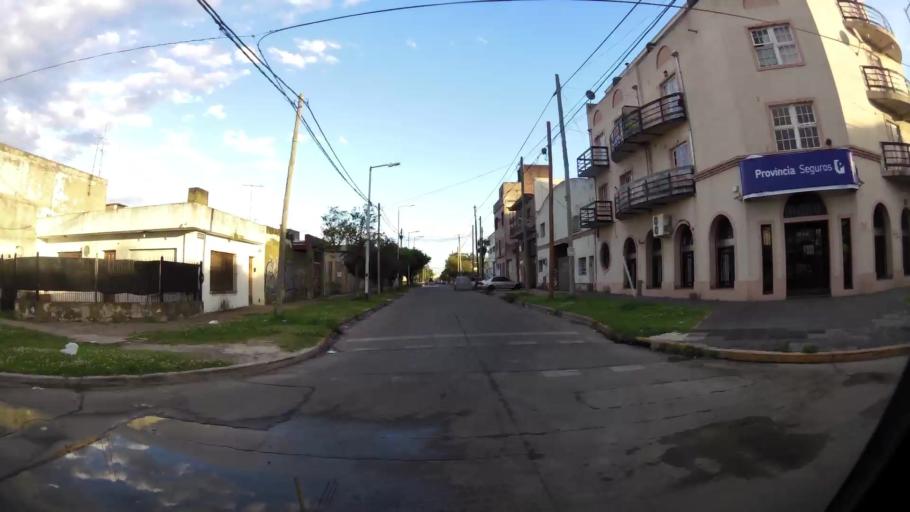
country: AR
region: Buenos Aires
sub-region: Partido de Avellaneda
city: Avellaneda
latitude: -34.6990
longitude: -58.3358
